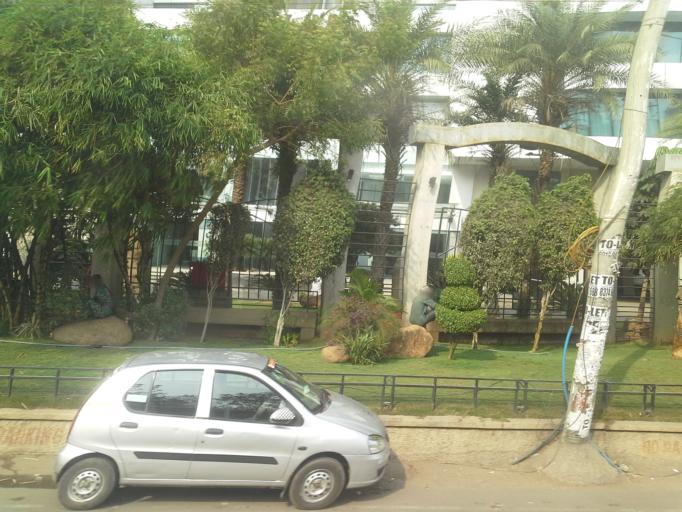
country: IN
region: Telangana
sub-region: Rangareddi
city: Kukatpalli
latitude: 17.4583
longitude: 78.3704
